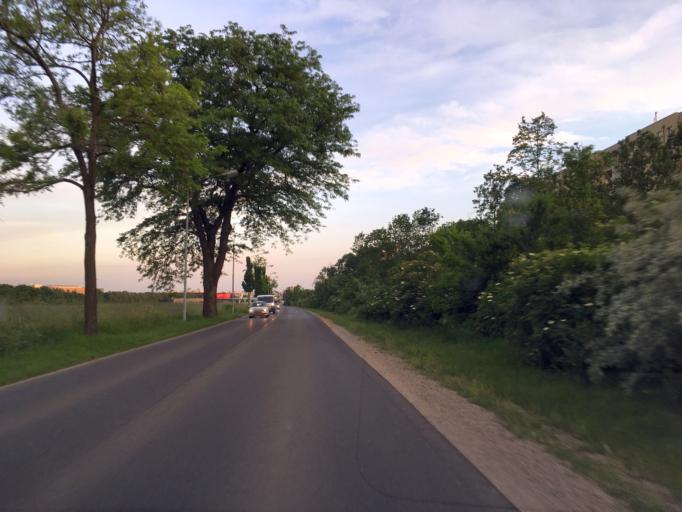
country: AT
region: Lower Austria
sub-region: Politischer Bezirk Wien-Umgebung
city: Gerasdorf bei Wien
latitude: 48.2726
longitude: 16.4570
